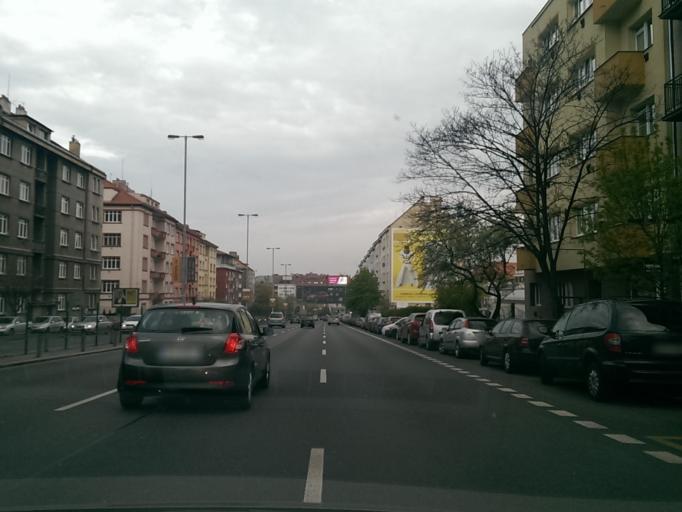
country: CZ
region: Praha
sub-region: Praha 2
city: Vysehrad
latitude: 50.0547
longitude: 14.4389
